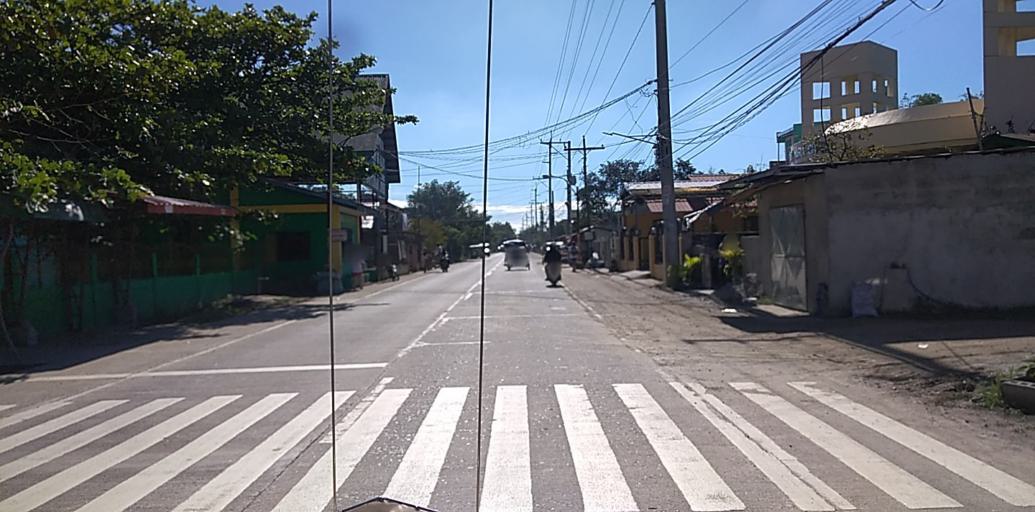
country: PH
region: Central Luzon
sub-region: Province of Pampanga
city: Santo Domingo
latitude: 15.0596
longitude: 120.7737
